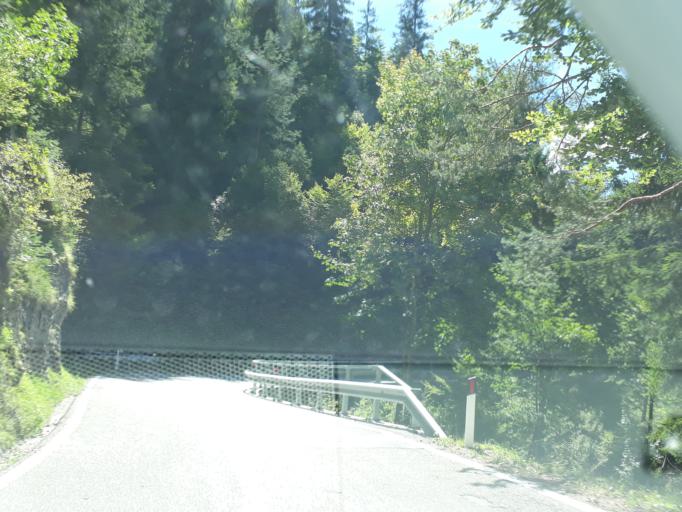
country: IT
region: Trentino-Alto Adige
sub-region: Provincia di Trento
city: Cimego
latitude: 45.8686
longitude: 10.6595
